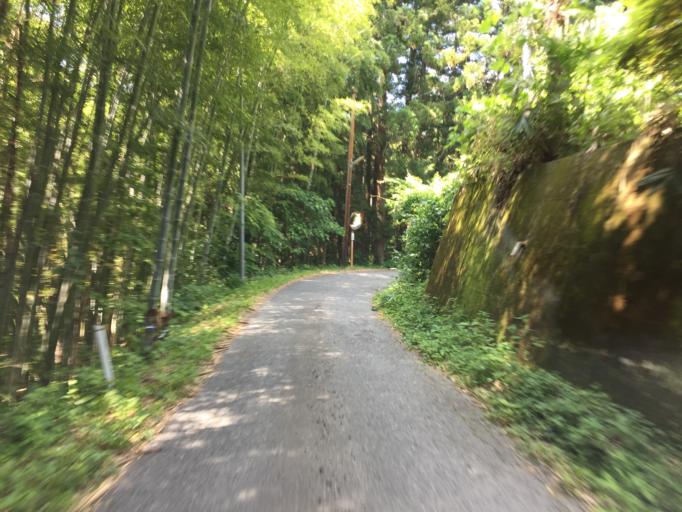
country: JP
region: Fukushima
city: Yanagawamachi-saiwaicho
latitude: 37.7782
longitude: 140.6550
